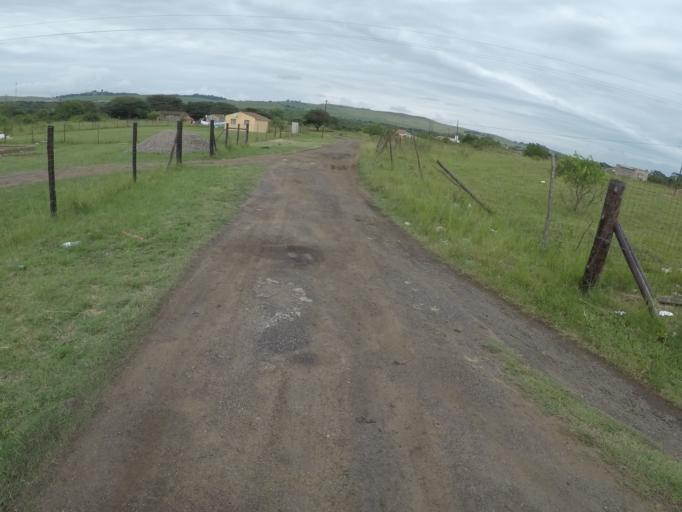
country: ZA
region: KwaZulu-Natal
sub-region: uThungulu District Municipality
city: Empangeni
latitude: -28.7128
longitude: 31.8641
